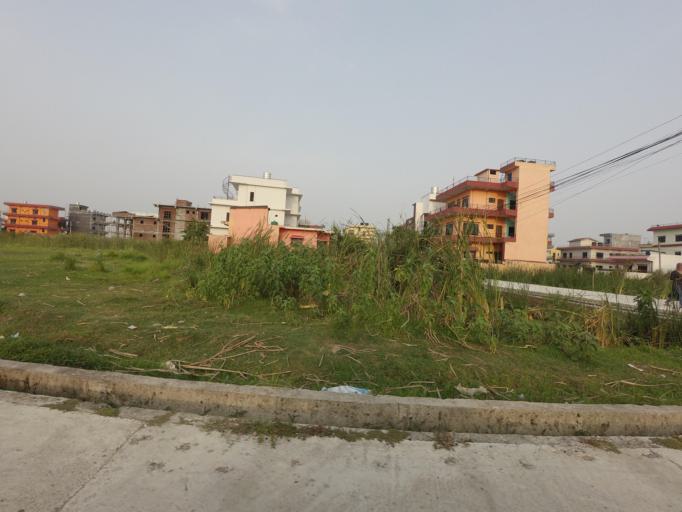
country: NP
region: Western Region
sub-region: Lumbini Zone
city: Bhairahawa
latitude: 27.5130
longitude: 83.4592
